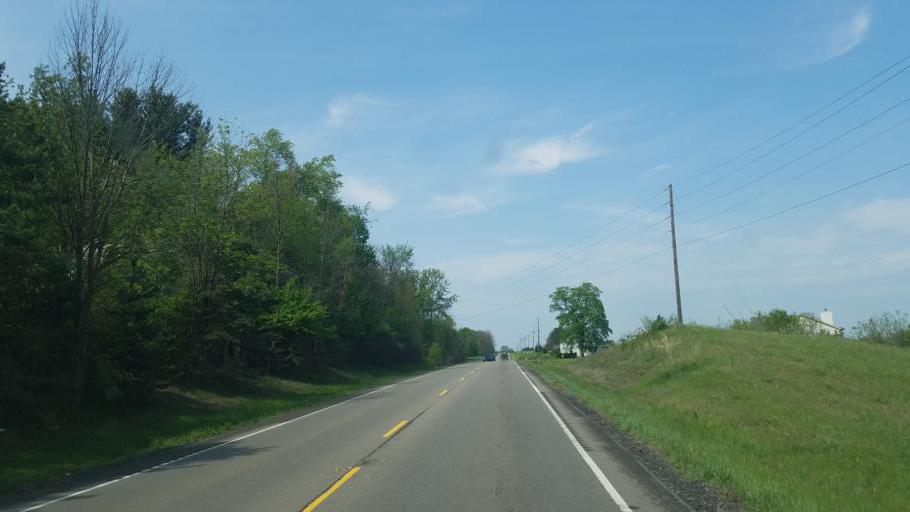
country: US
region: Ohio
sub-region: Licking County
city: Hebron
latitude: 39.9959
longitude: -82.5247
